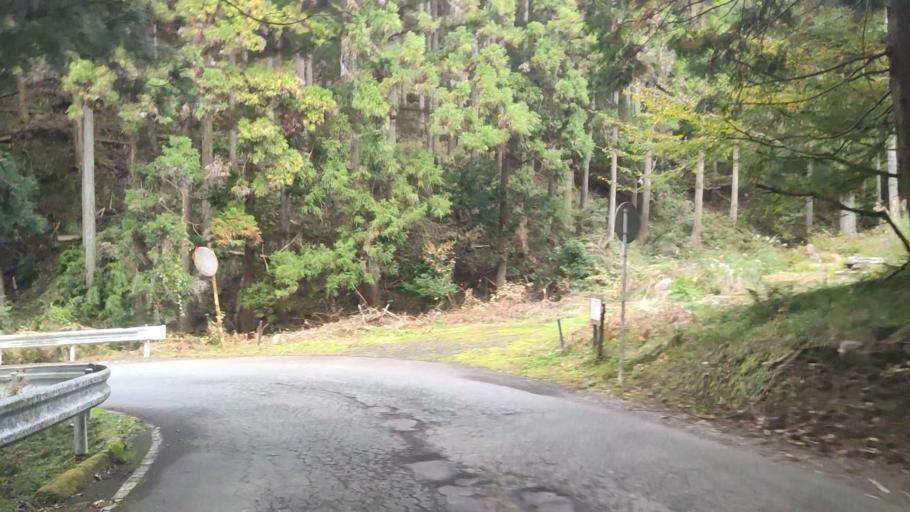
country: JP
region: Shizuoka
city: Ito
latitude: 34.9542
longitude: 139.0436
